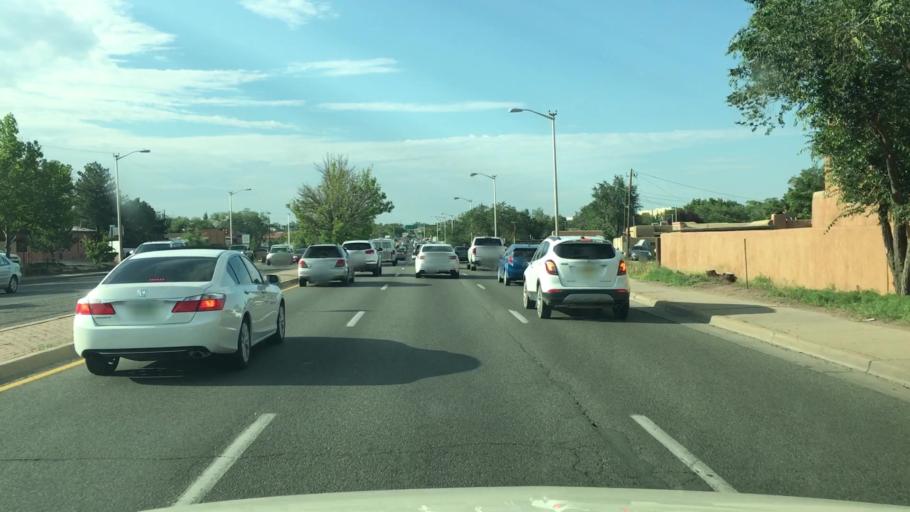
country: US
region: New Mexico
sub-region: Santa Fe County
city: Santa Fe
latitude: 35.6814
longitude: -105.9548
